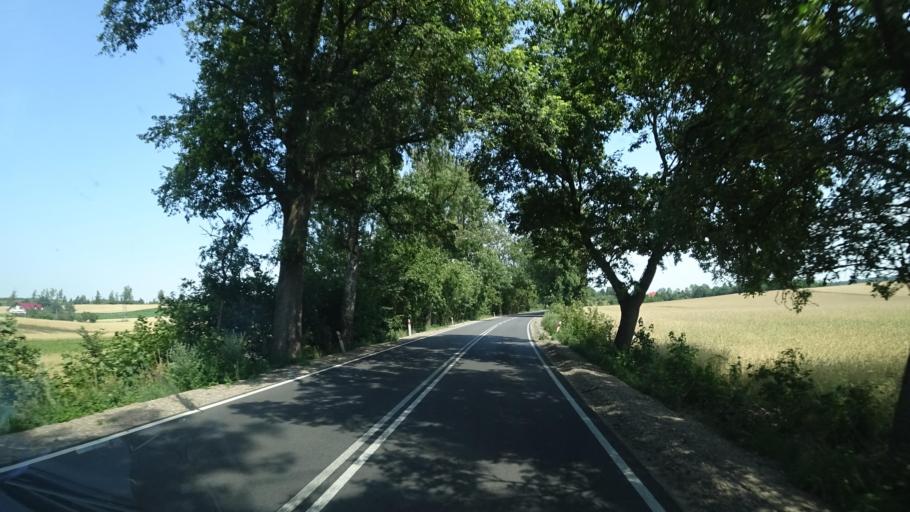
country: PL
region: Pomeranian Voivodeship
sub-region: Powiat koscierski
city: Dziemiany
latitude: 53.9643
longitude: 17.7508
